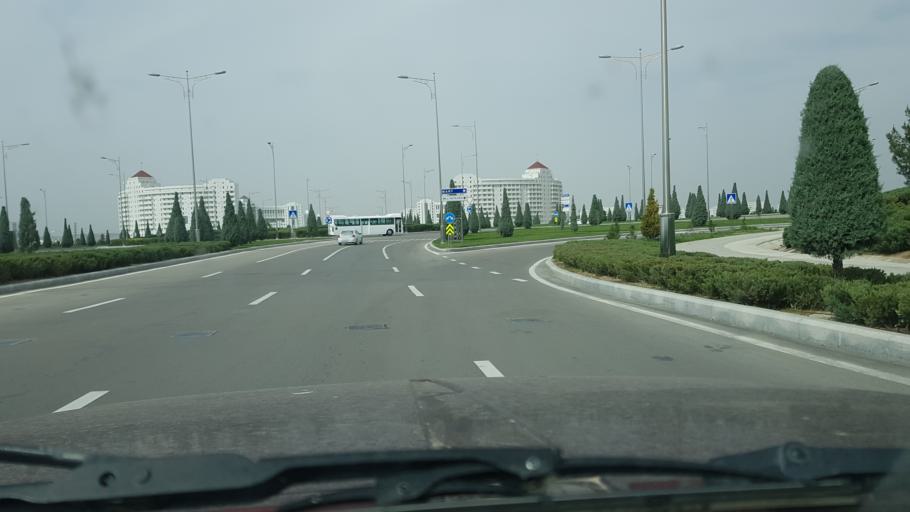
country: TM
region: Ahal
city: Ashgabat
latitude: 37.8873
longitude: 58.3341
